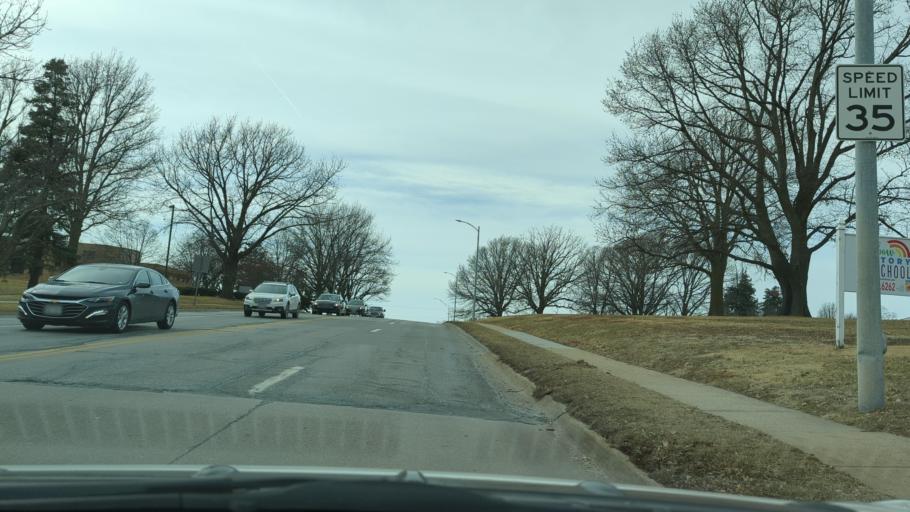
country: US
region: Nebraska
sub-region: Douglas County
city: Ralston
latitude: 41.2633
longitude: -96.0194
